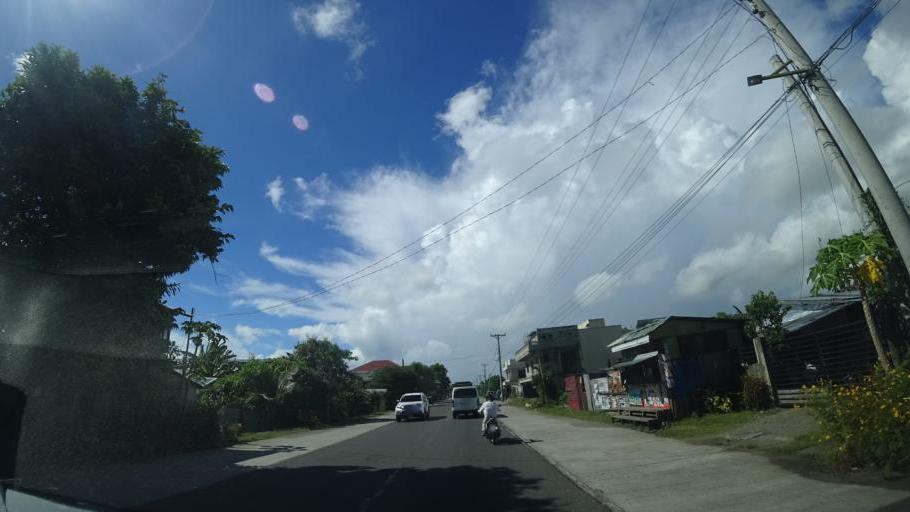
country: PH
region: Eastern Visayas
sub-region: Province of Leyte
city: Palo
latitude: 11.1400
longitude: 125.0053
